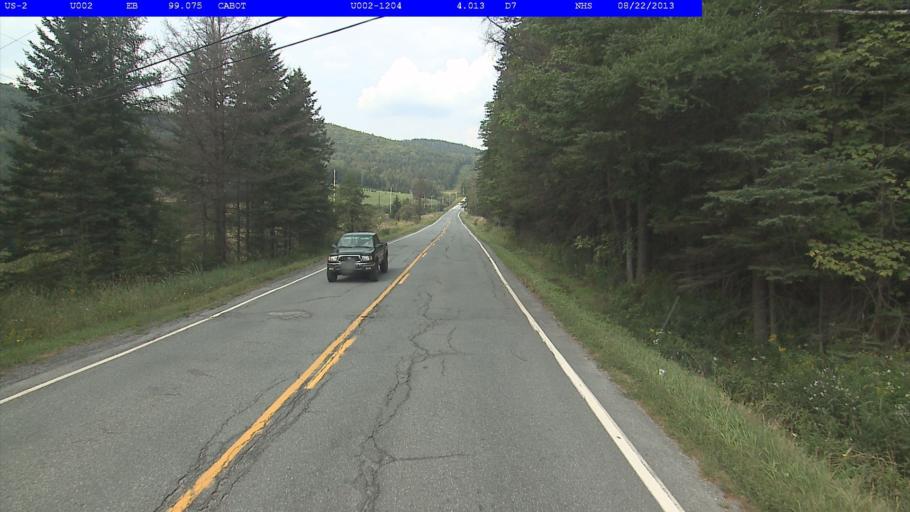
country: US
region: Vermont
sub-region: Caledonia County
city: Hardwick
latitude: 44.3824
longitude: -72.2571
